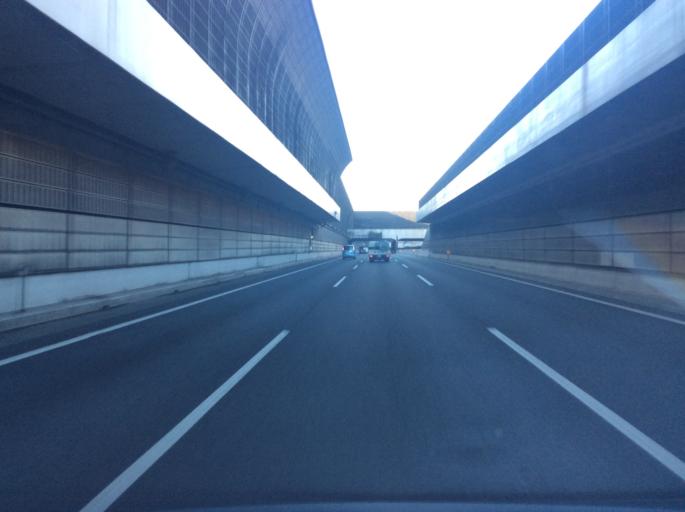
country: JP
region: Chiba
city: Nagareyama
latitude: 35.8891
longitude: 139.9139
